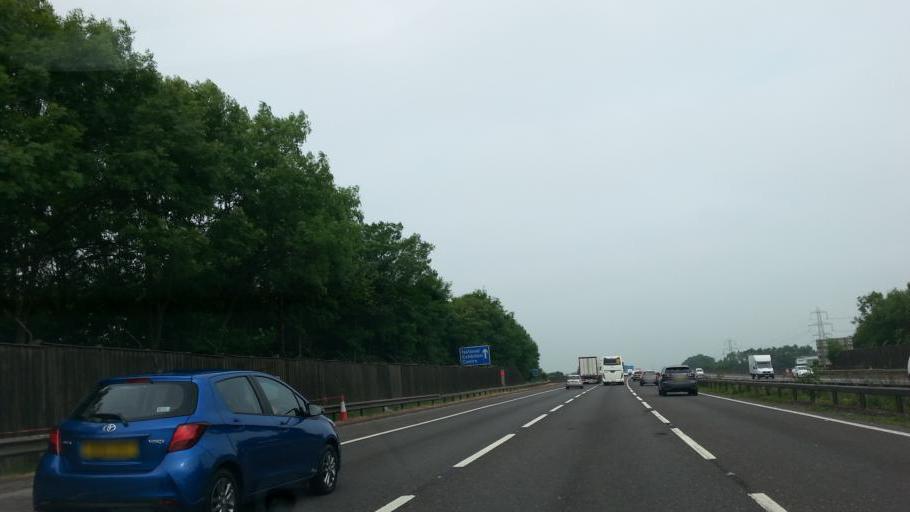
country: GB
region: England
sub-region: Warwickshire
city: Exhall
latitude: 52.4556
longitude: -1.4781
